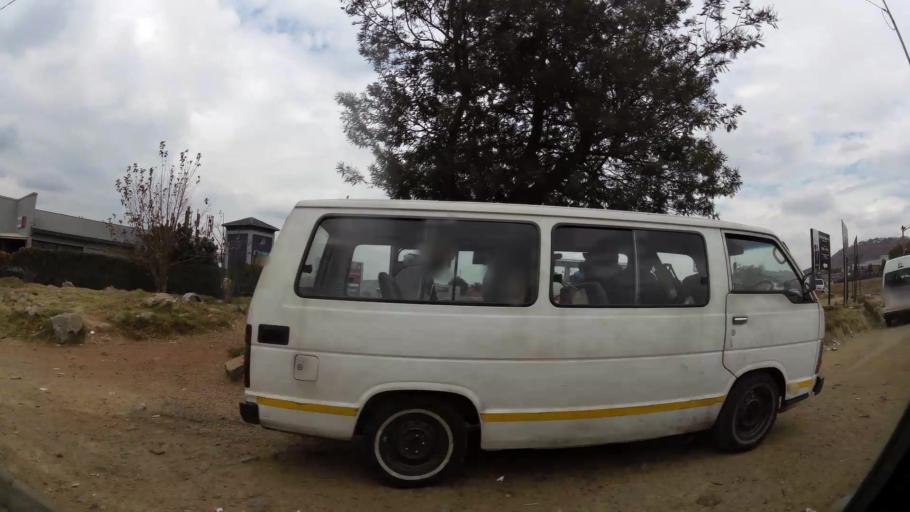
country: ZA
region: Gauteng
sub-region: West Rand District Municipality
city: Muldersdriseloop
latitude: -26.0914
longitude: 27.8698
